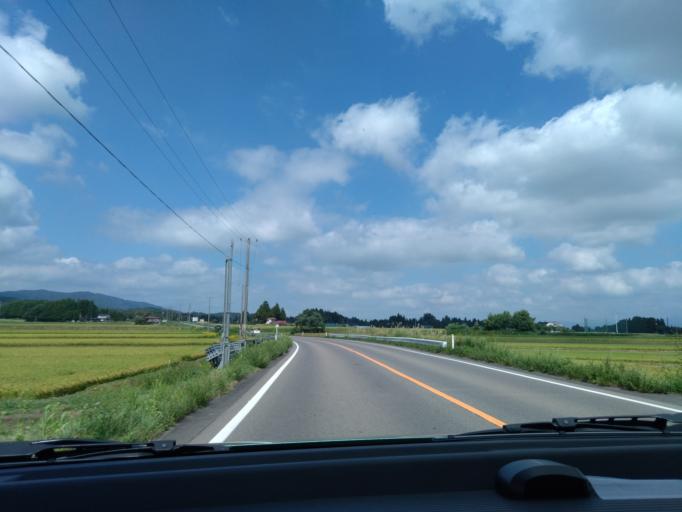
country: JP
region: Iwate
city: Hanamaki
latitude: 39.4622
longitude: 141.1017
